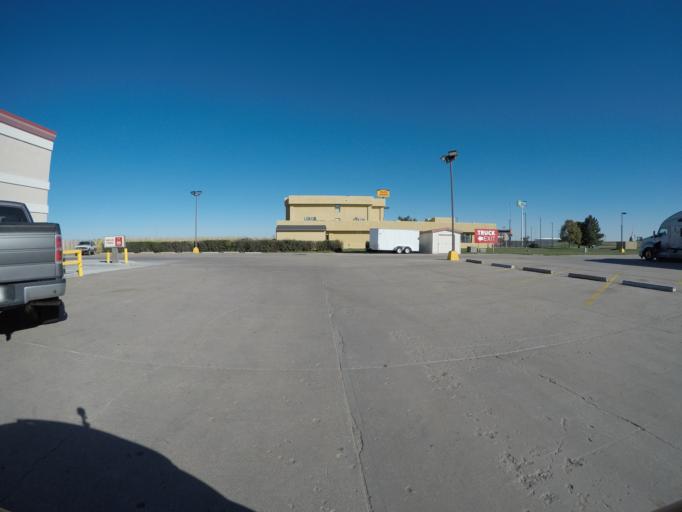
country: US
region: Kansas
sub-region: Thomas County
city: Colby
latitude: 39.3667
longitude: -101.0537
